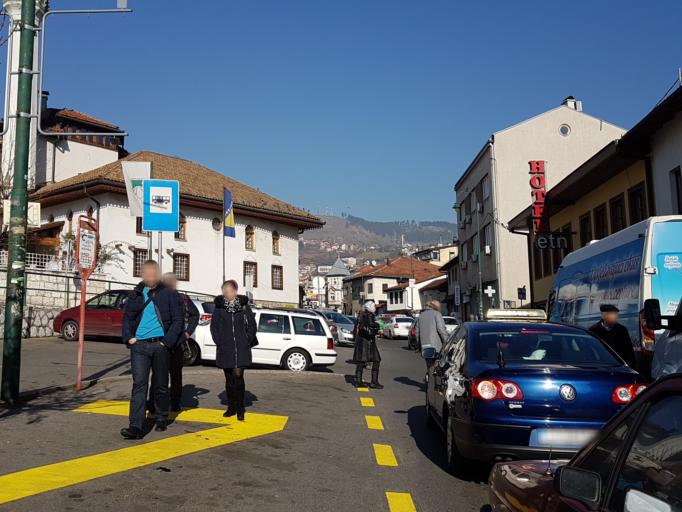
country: BA
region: Federation of Bosnia and Herzegovina
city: Kobilja Glava
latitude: 43.8606
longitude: 18.4315
